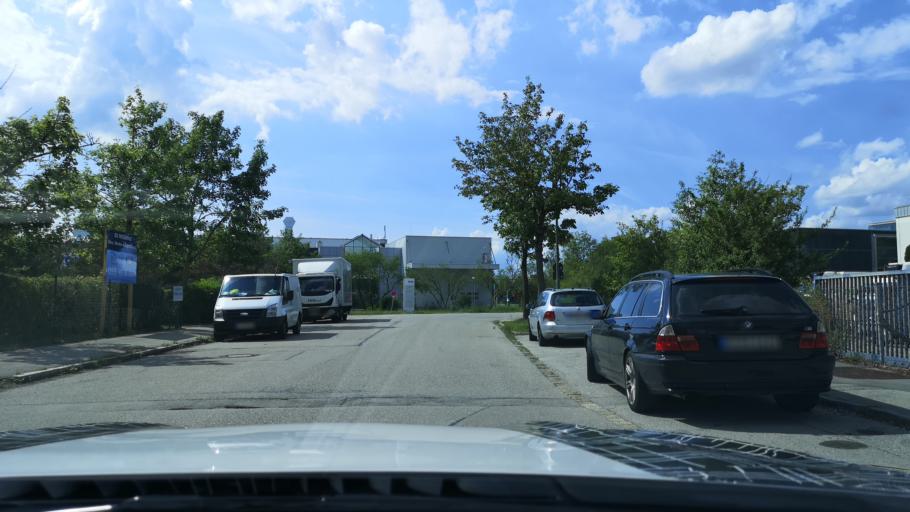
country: DE
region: Bavaria
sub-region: Upper Bavaria
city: Garching bei Munchen
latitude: 48.2483
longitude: 11.6199
